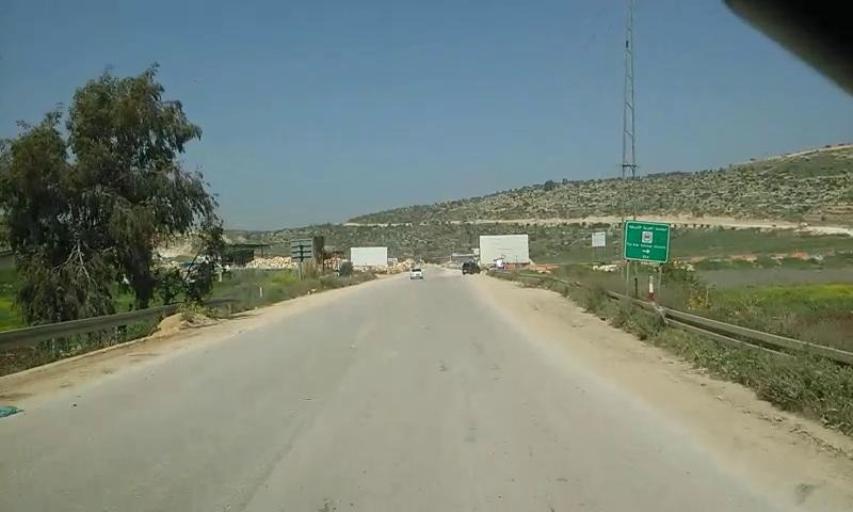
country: PS
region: West Bank
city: Az Zababidah
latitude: 32.3996
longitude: 35.3183
